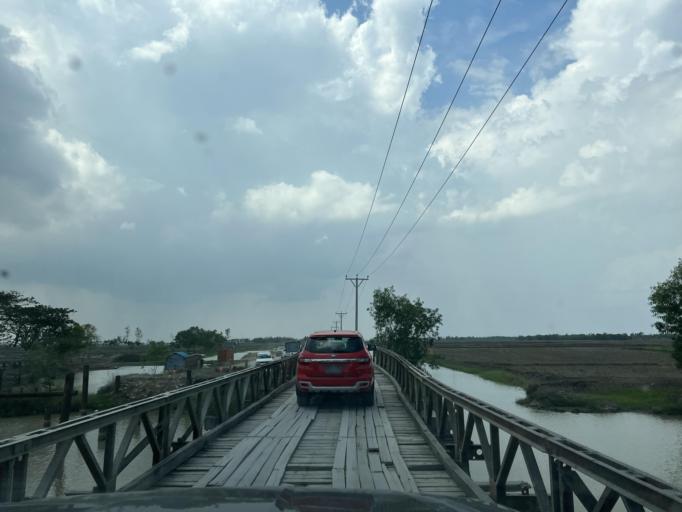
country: MM
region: Ayeyarwady
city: Pyapon
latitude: 16.0505
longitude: 95.6141
